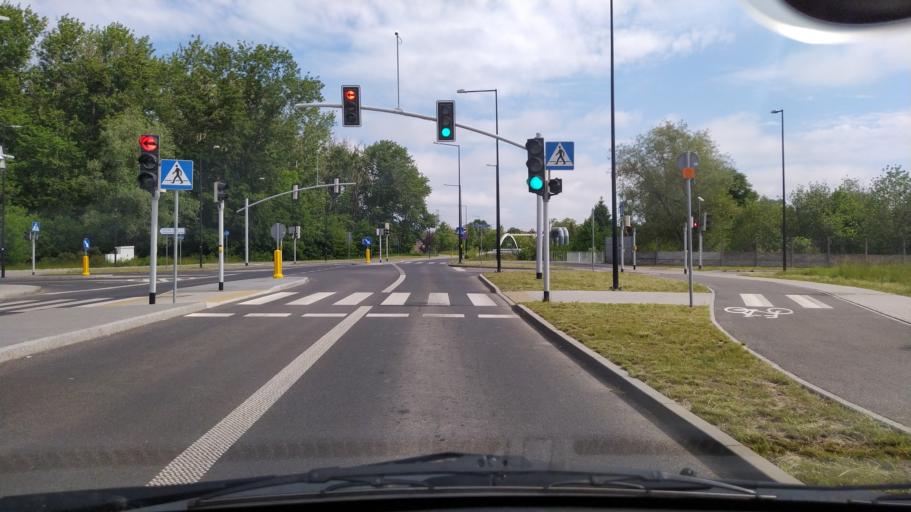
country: PL
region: Silesian Voivodeship
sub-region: Gliwice
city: Gliwice
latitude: 50.2855
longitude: 18.6922
